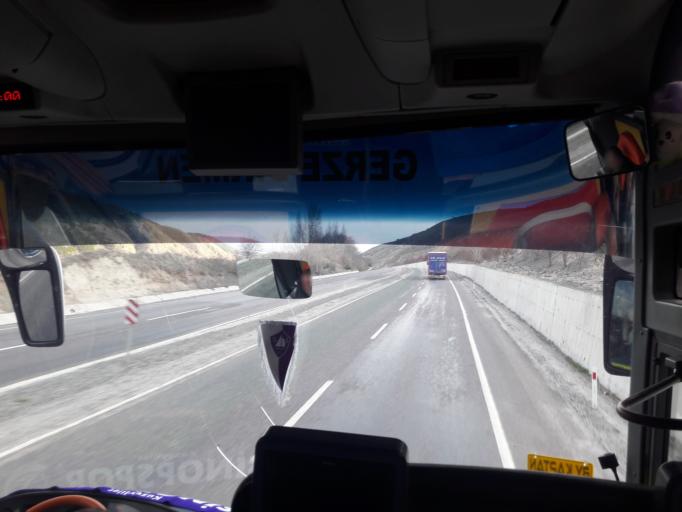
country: TR
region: Cankiri
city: Korgun
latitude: 40.7603
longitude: 33.5269
